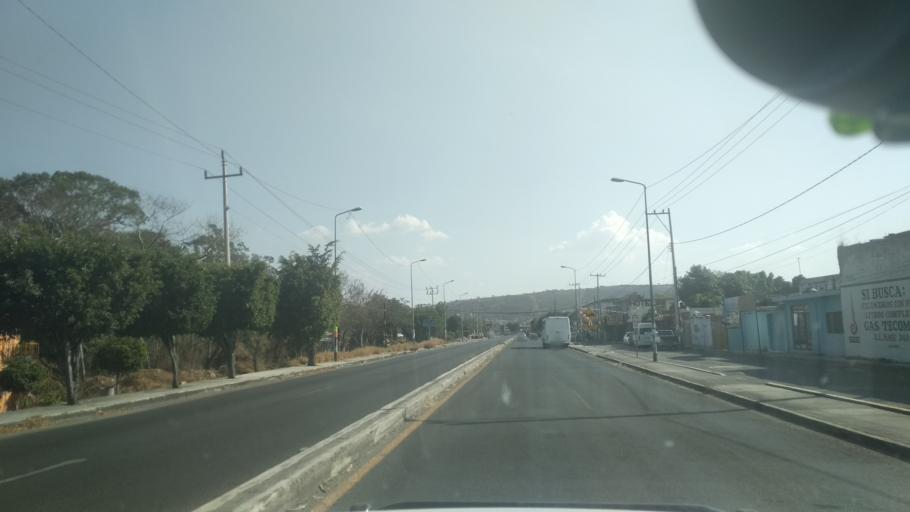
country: MX
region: Puebla
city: Izucar de Matamoros
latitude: 18.6252
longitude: -98.4699
